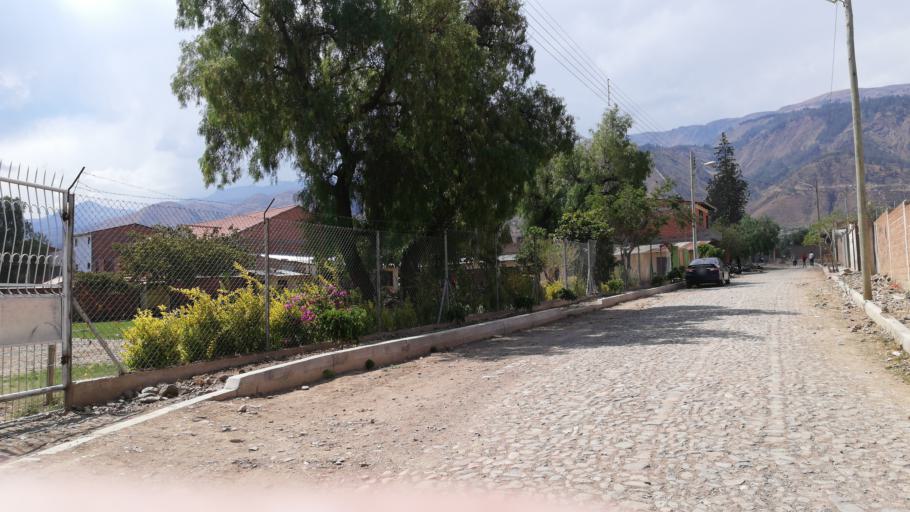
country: BO
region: Cochabamba
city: Cochabamba
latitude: -17.3337
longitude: -66.2209
